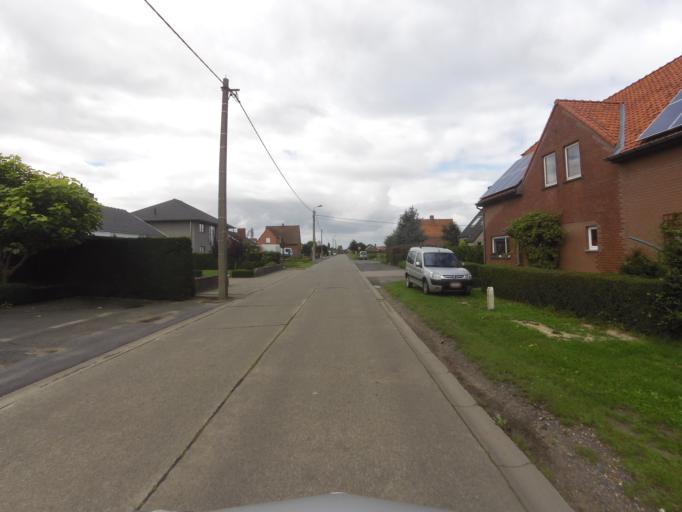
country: BE
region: Flanders
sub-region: Provincie West-Vlaanderen
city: Wingene
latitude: 51.0559
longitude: 3.2965
